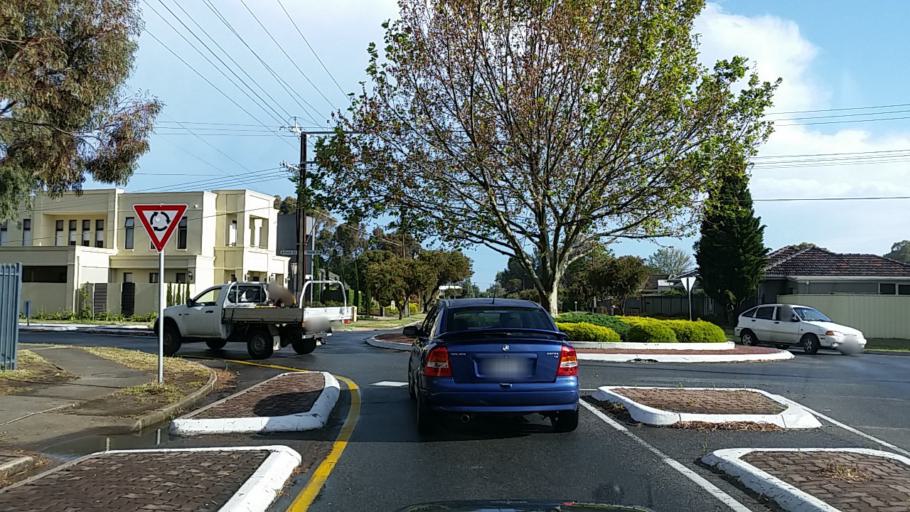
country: AU
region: South Australia
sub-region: Charles Sturt
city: Henley Beach
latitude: -34.9162
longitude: 138.5005
